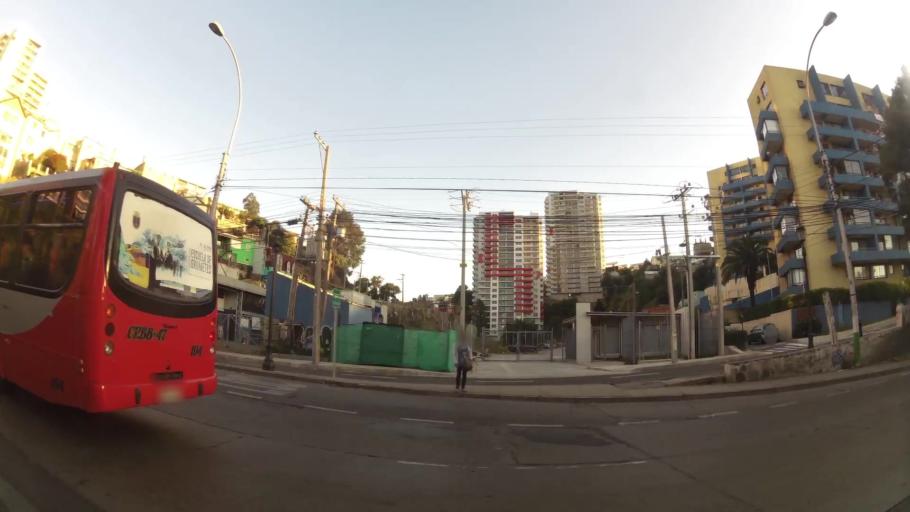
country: CL
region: Valparaiso
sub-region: Provincia de Valparaiso
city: Valparaiso
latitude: -33.0376
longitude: -71.5983
